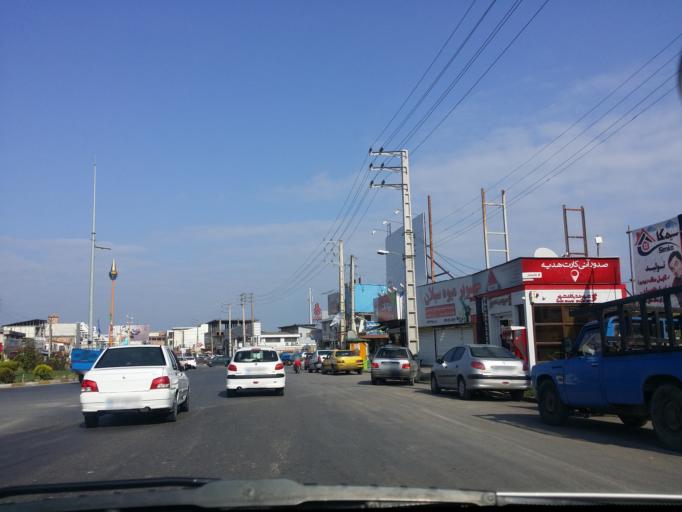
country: IR
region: Mazandaran
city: Chalus
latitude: 36.6818
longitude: 51.4023
